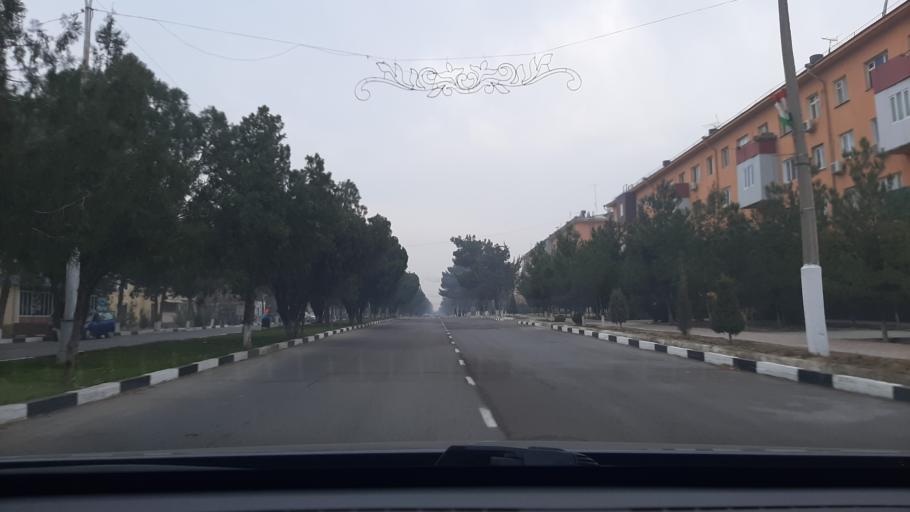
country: TJ
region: Viloyati Sughd
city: Chkalov
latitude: 40.2331
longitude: 69.6887
